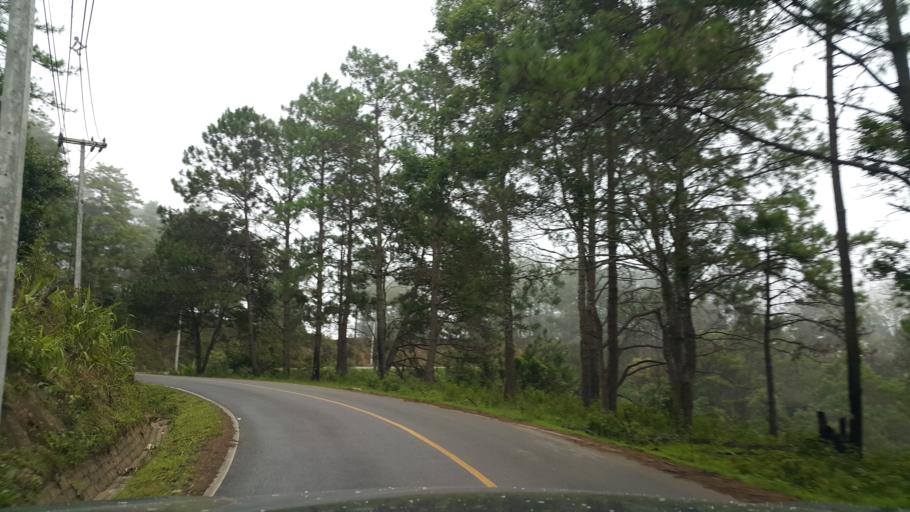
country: TH
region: Chiang Mai
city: Samoeng
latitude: 18.8810
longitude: 98.5242
